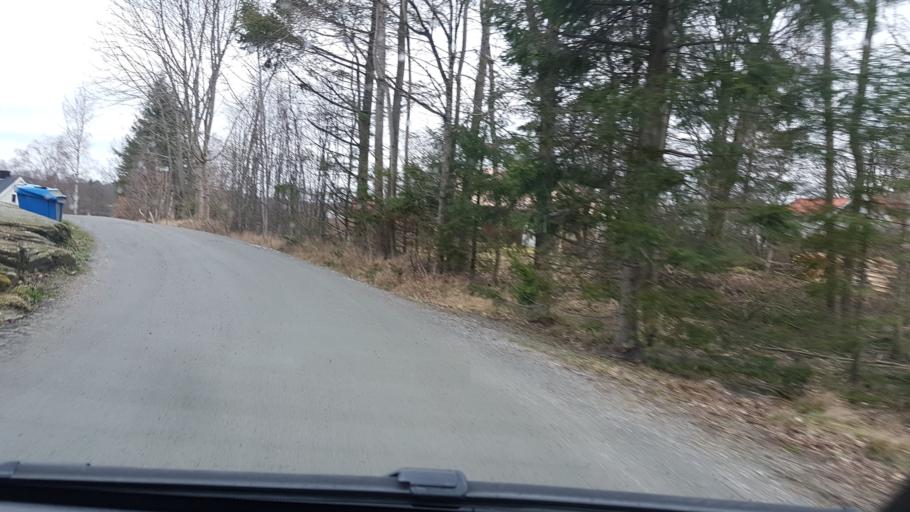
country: SE
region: Vaestra Goetaland
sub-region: Lerums Kommun
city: Stenkullen
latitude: 57.8022
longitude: 12.3812
